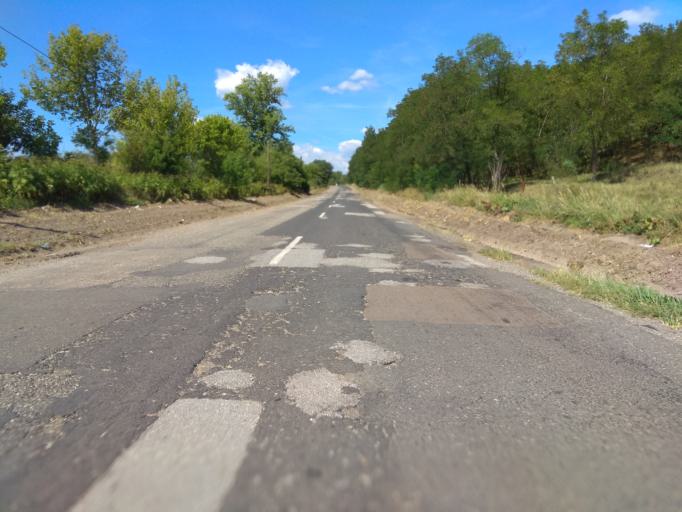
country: HU
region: Borsod-Abauj-Zemplen
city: Kazincbarcika
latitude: 48.2814
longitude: 20.6382
